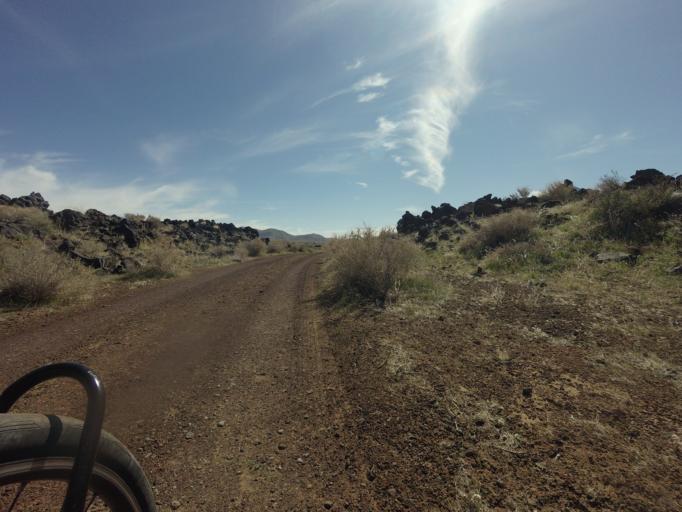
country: US
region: California
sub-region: Kern County
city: Inyokern
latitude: 35.9758
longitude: -117.9118
